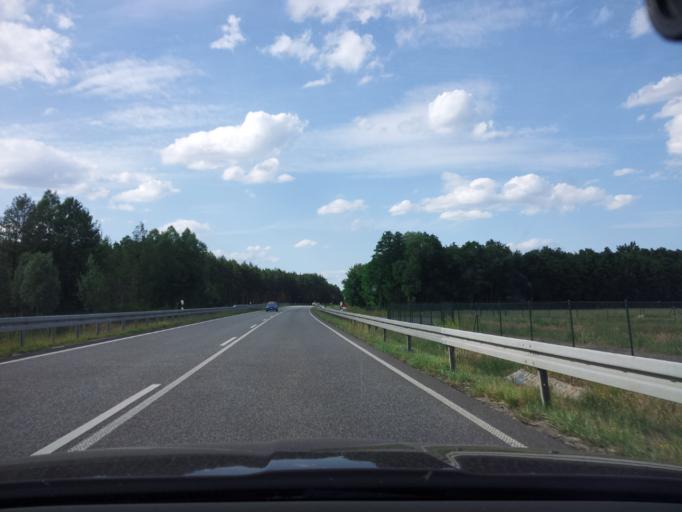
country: DE
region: Brandenburg
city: Juterbog
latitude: 52.0422
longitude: 13.1044
